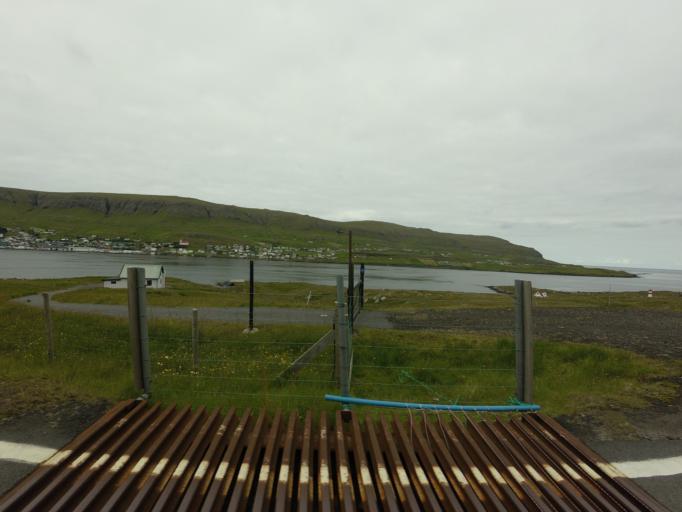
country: FO
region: Suduroy
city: Tvoroyri
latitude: 61.5432
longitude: -6.8085
